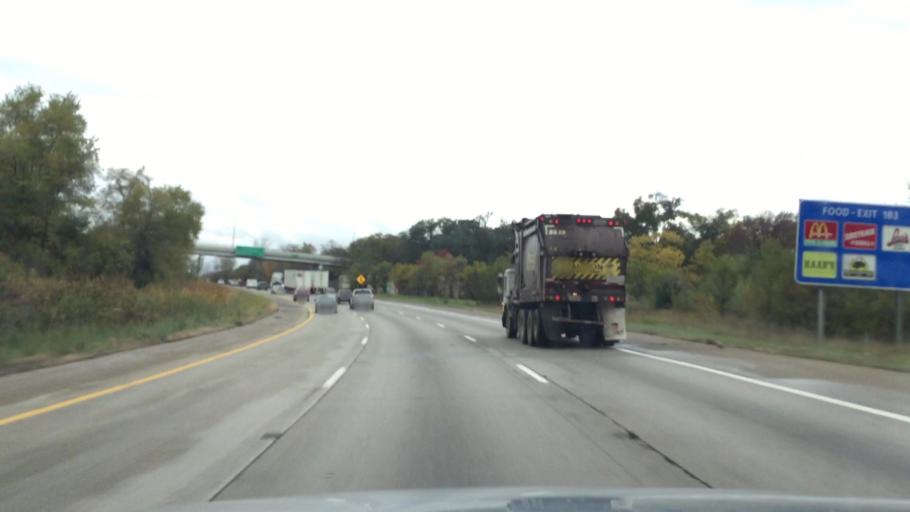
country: US
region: Michigan
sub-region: Washtenaw County
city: Ypsilanti
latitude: 42.2316
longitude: -83.5792
